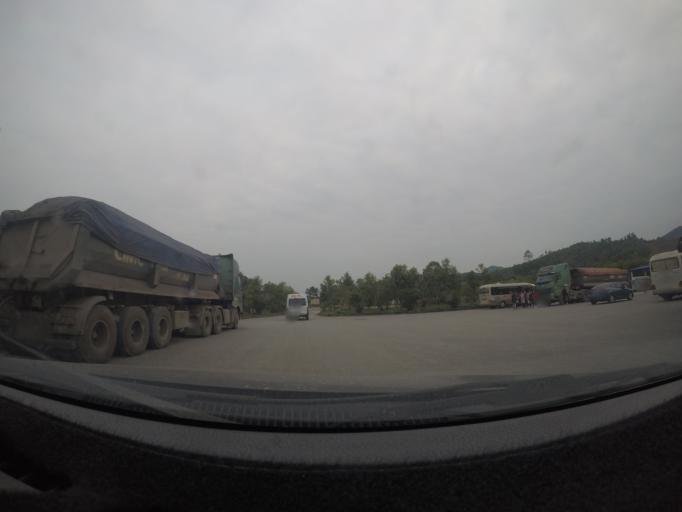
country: VN
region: Yen Bai
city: Yen Bai
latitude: 21.6735
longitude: 104.8787
